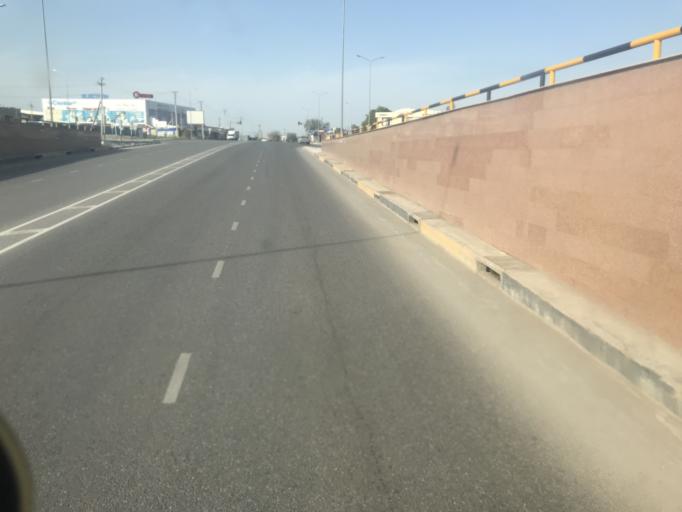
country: KZ
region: Ongtustik Qazaqstan
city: Shymkent
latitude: 42.3531
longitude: 69.5319
